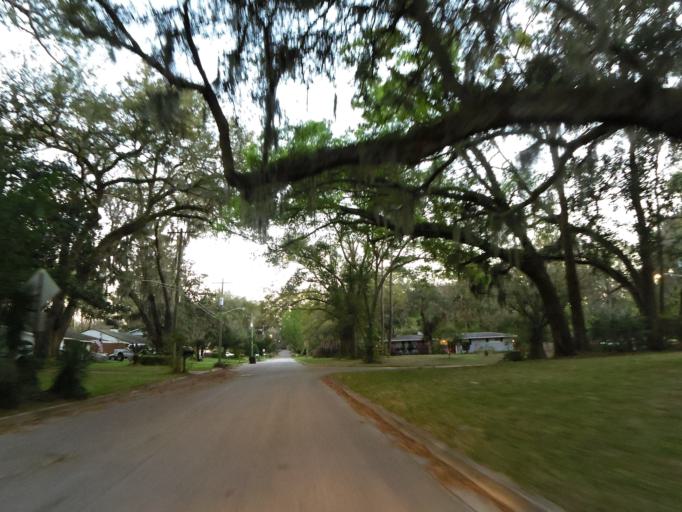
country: US
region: Florida
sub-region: Clay County
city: Orange Park
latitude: 30.1590
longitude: -81.7017
